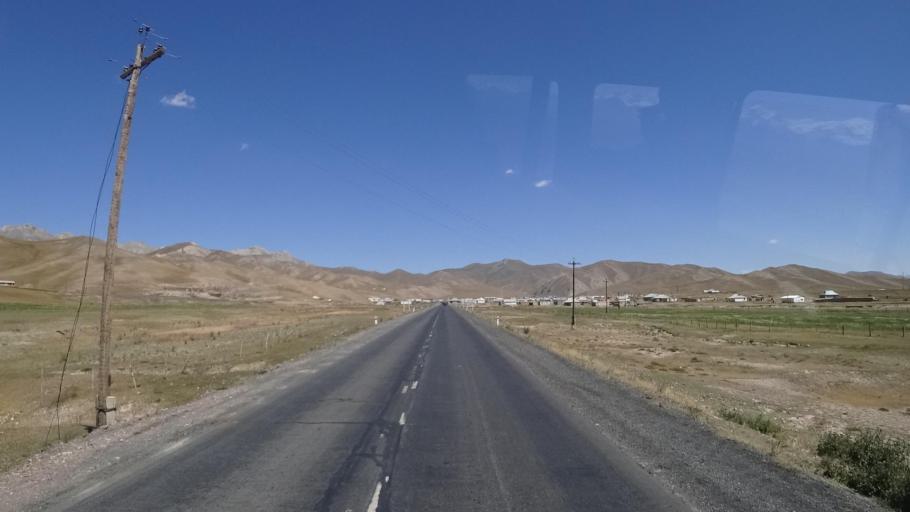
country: KG
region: Osh
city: Gul'cha
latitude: 39.7183
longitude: 73.2431
